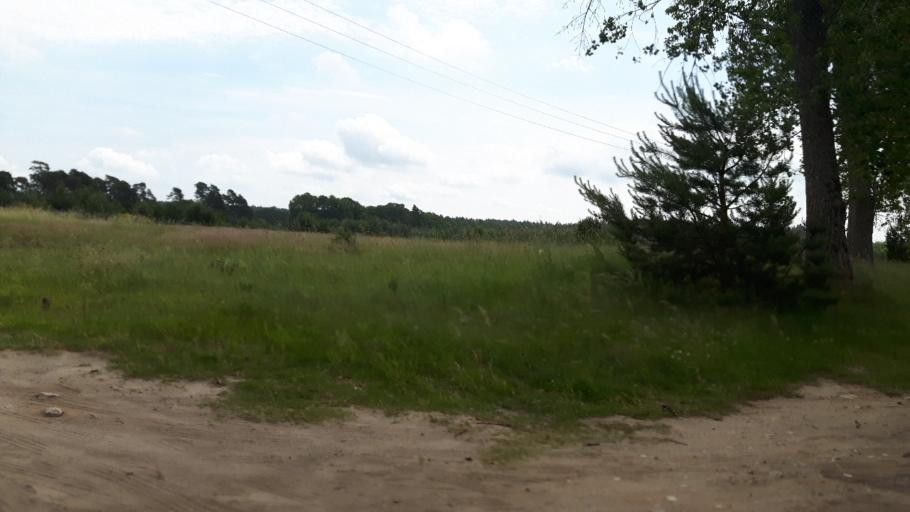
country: PL
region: Pomeranian Voivodeship
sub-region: Powiat leborski
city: Leba
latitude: 54.7539
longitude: 17.7099
